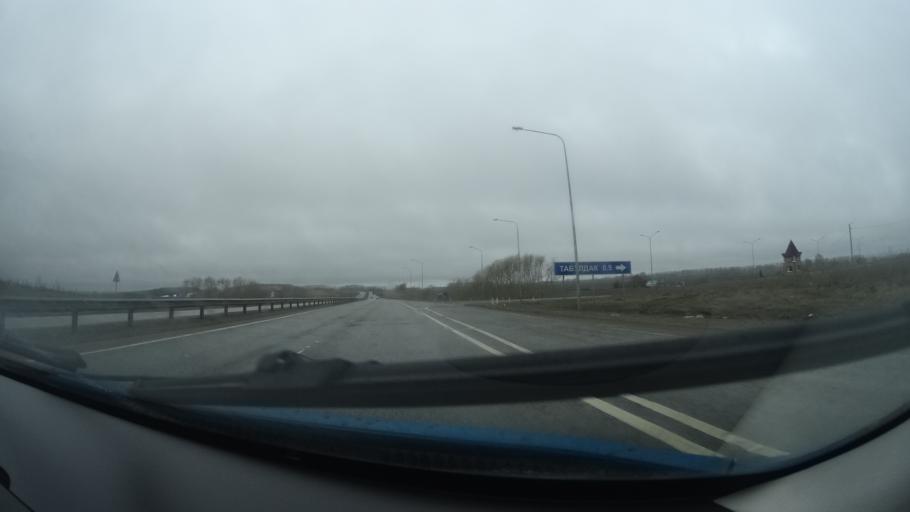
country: RU
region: Bashkortostan
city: Alekseyevka
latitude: 54.7372
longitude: 55.1140
